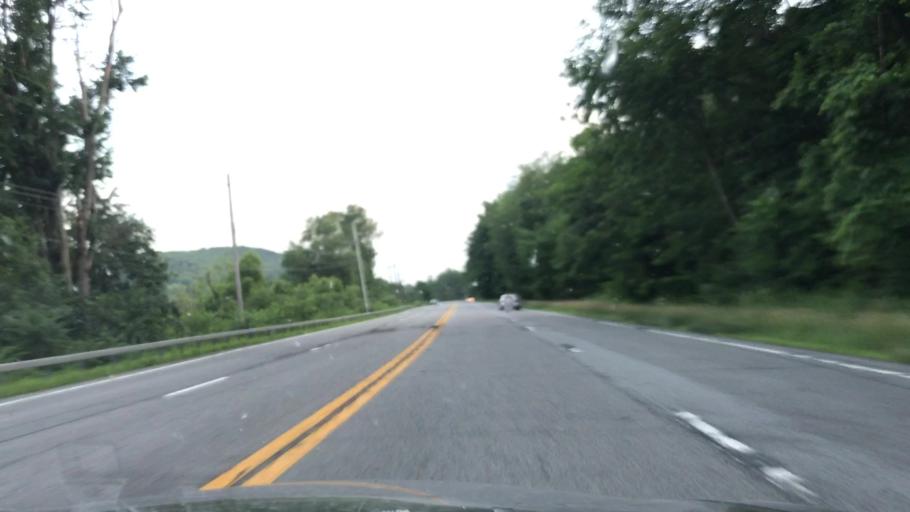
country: US
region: New York
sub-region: Orange County
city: Harriman
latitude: 41.2846
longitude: -74.1463
